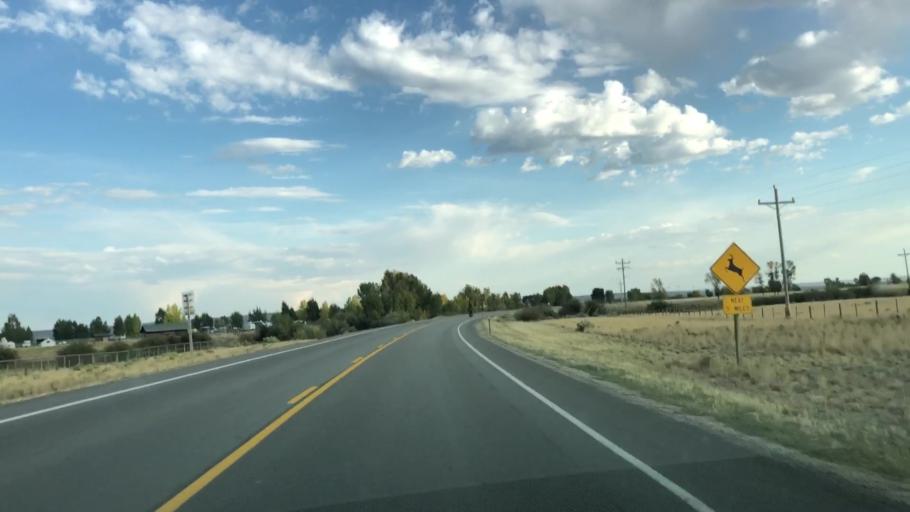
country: US
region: Wyoming
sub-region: Sublette County
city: Pinedale
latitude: 42.7417
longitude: -109.7166
